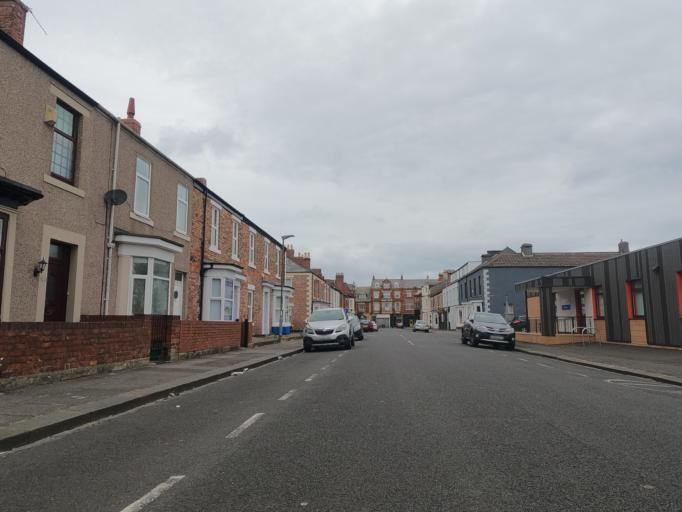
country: GB
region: England
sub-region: Northumberland
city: Blyth
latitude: 55.1263
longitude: -1.5055
